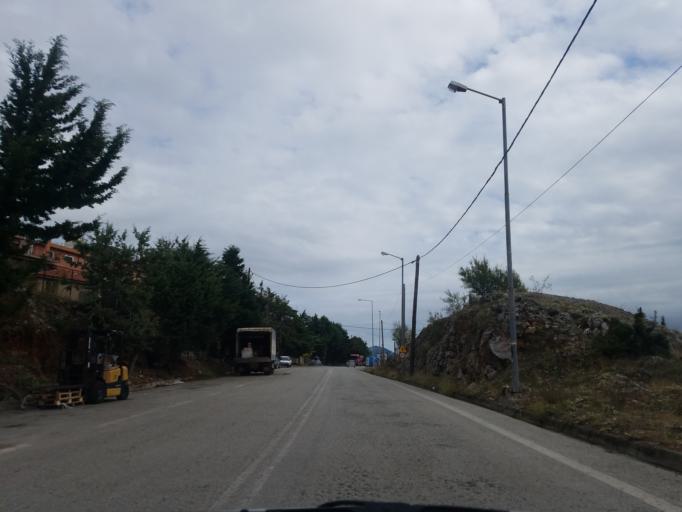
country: GR
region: Central Greece
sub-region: Nomos Voiotias
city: Arachova
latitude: 38.4807
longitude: 22.5773
